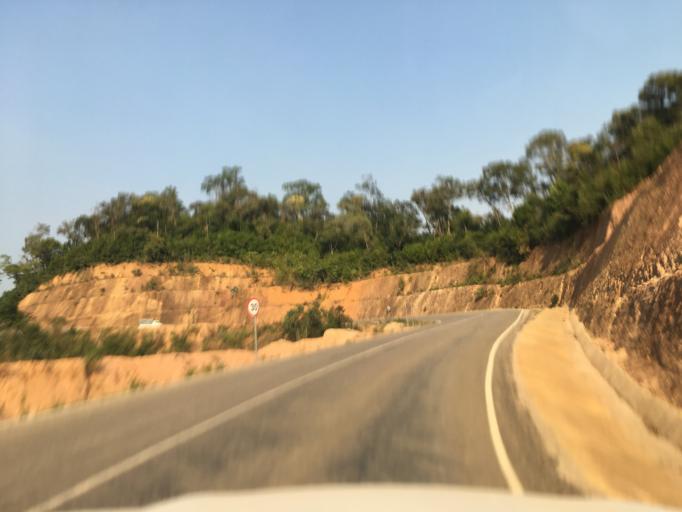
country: LA
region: Houaphan
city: Xam Nua
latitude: 20.5848
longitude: 104.0567
